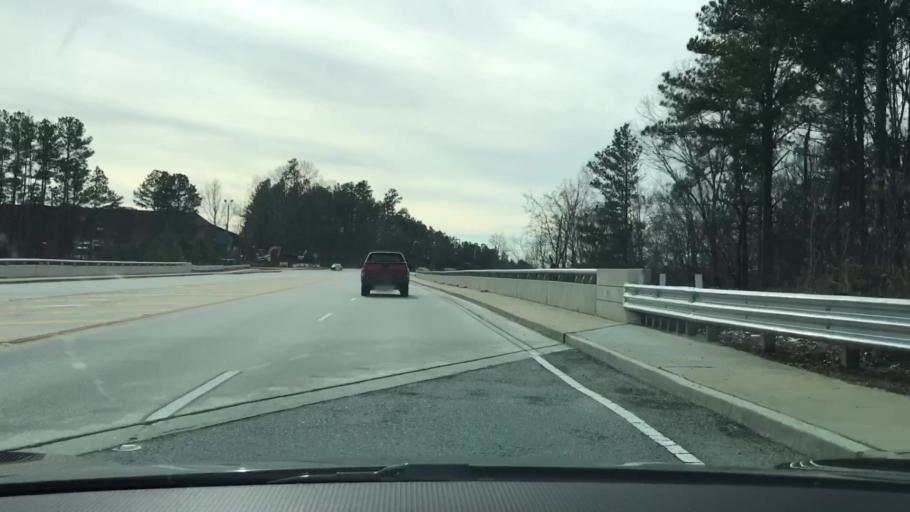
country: US
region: Georgia
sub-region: Gwinnett County
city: Suwanee
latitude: 34.0192
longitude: -84.0572
